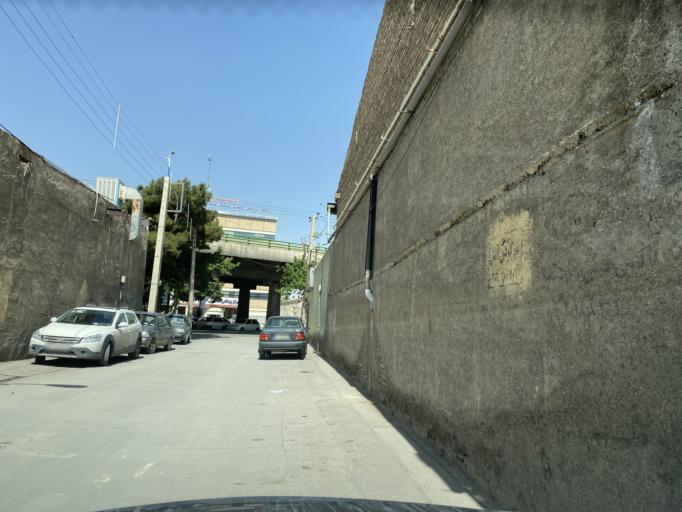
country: IR
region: Isfahan
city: Rehnan
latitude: 32.6924
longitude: 51.6265
